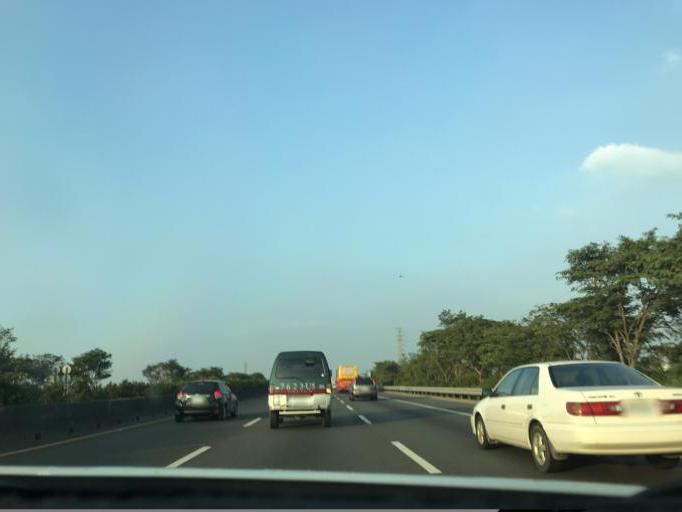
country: TW
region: Taiwan
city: Xinying
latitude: 23.2931
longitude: 120.2817
